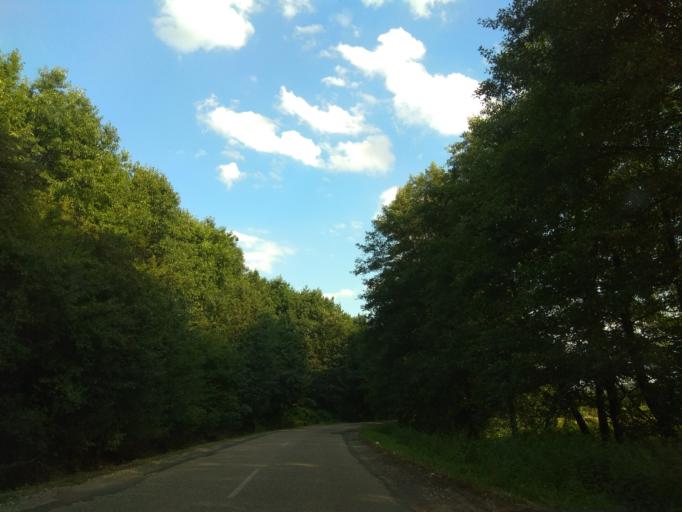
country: HU
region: Borsod-Abauj-Zemplen
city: Harsany
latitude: 47.9972
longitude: 20.7605
